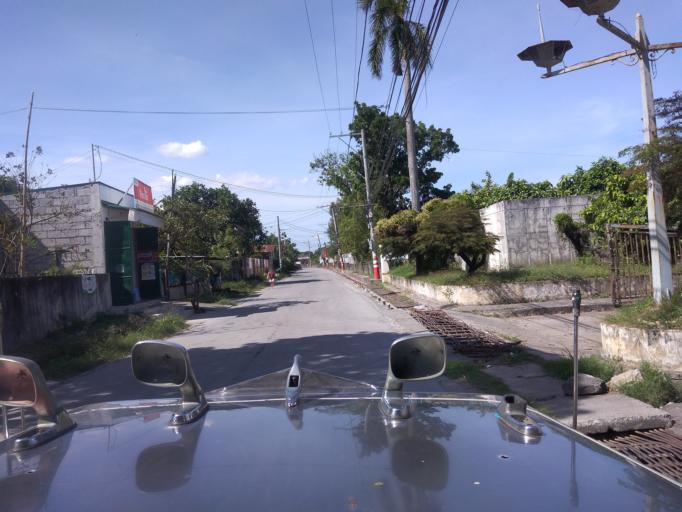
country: PH
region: Central Luzon
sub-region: Province of Pampanga
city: Magliman
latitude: 15.0320
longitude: 120.6672
